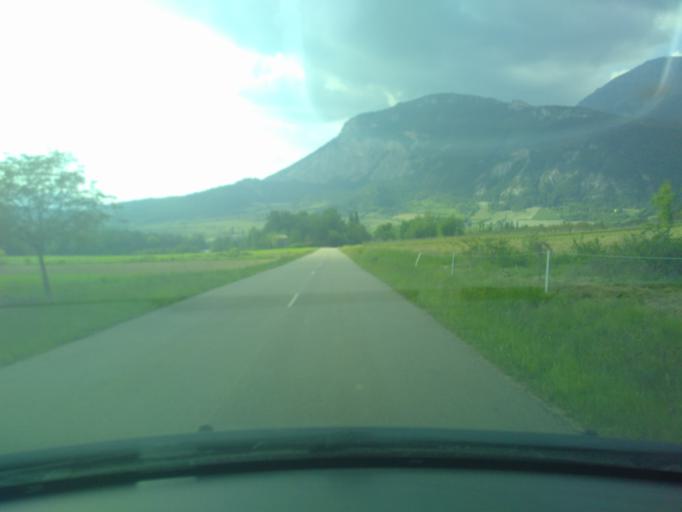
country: FR
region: Rhone-Alpes
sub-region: Departement de la Drome
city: Die
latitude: 44.6782
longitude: 5.4716
